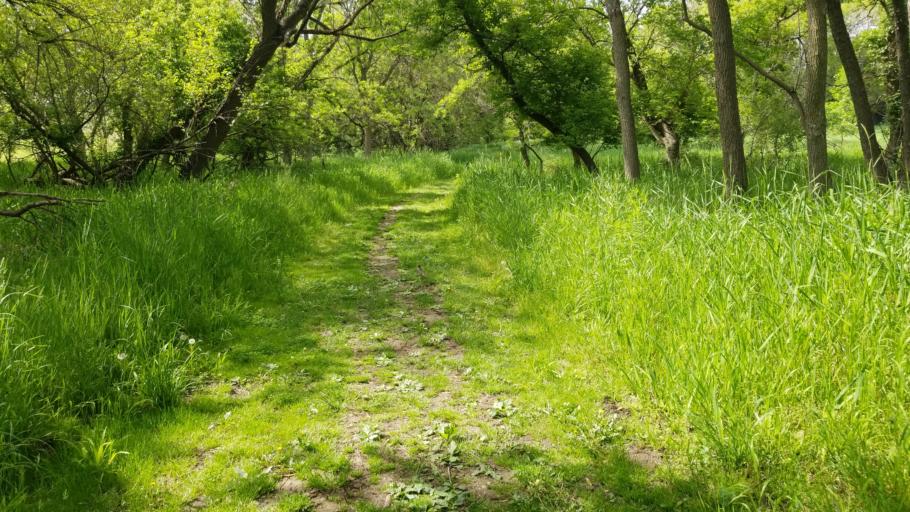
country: US
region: Nebraska
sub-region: Sarpy County
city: Chalco
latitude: 41.1714
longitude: -96.1653
